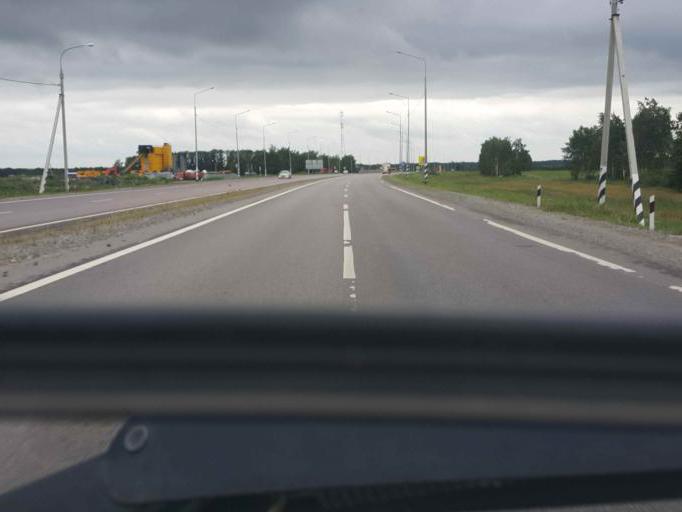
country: RU
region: Tambov
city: Zavoronezhskoye
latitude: 52.8576
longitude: 40.7739
